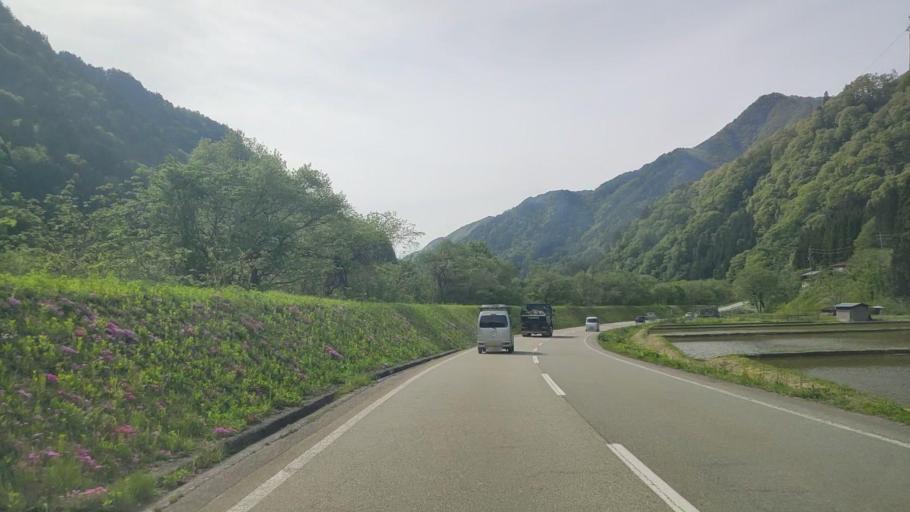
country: JP
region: Gifu
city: Takayama
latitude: 36.2611
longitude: 137.4329
